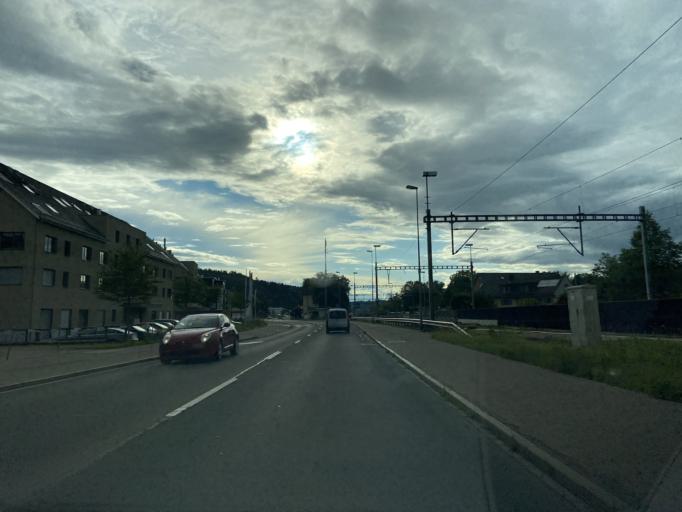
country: CH
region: Zurich
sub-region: Bezirk Winterthur
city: Elsau-Raeterschen / Raeterschen
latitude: 47.4982
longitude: 8.7973
